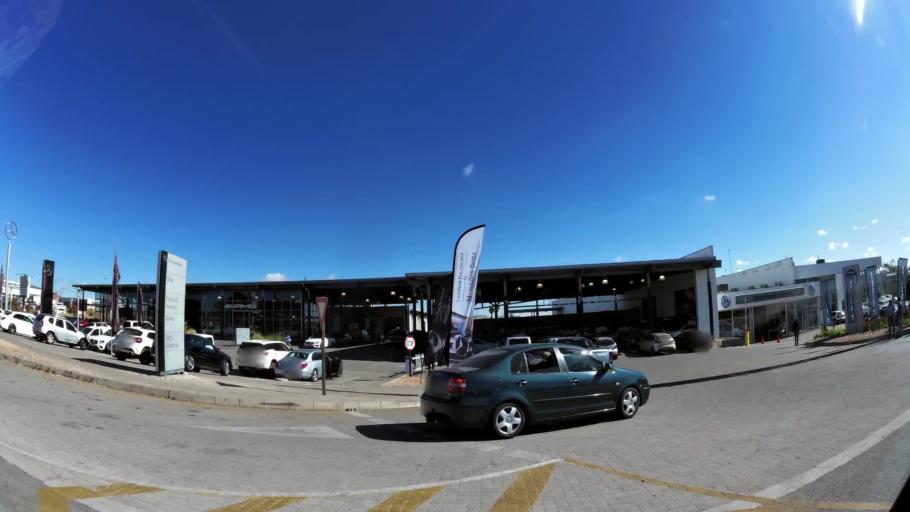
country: ZA
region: Limpopo
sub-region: Capricorn District Municipality
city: Polokwane
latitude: -23.9143
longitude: 29.4445
